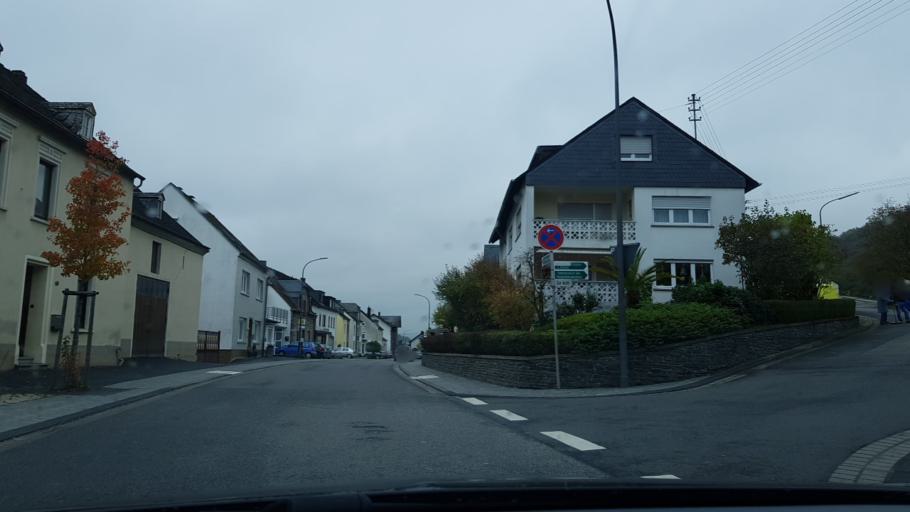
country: DE
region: Rheinland-Pfalz
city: Fell
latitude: 49.7735
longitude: 6.7811
